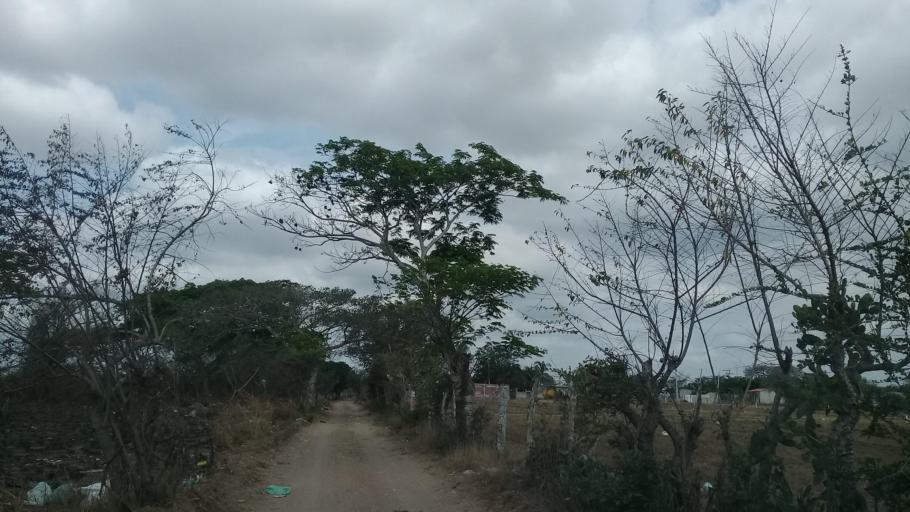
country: MX
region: Veracruz
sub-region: Veracruz
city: Las Amapolas
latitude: 19.1330
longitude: -96.2299
